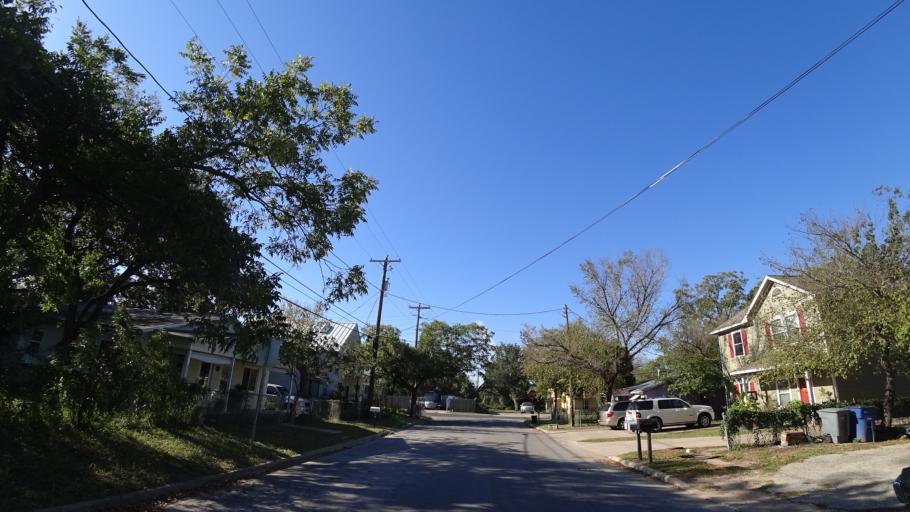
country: US
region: Texas
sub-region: Travis County
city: Austin
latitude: 30.2385
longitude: -97.6963
